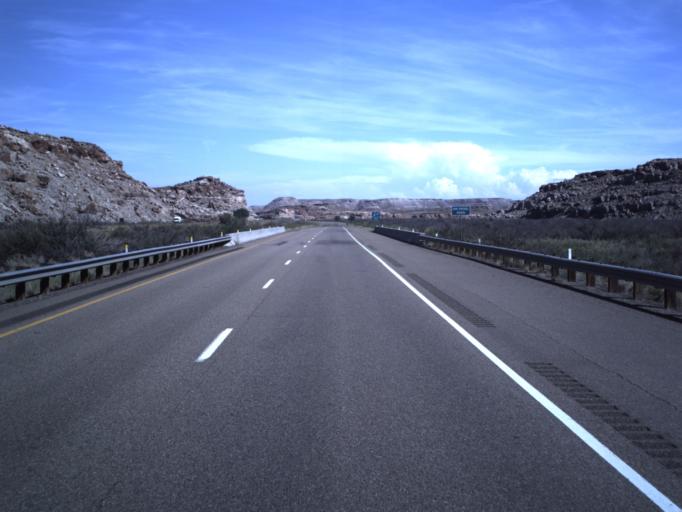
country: US
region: Utah
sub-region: Carbon County
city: East Carbon City
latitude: 38.9231
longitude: -110.4048
